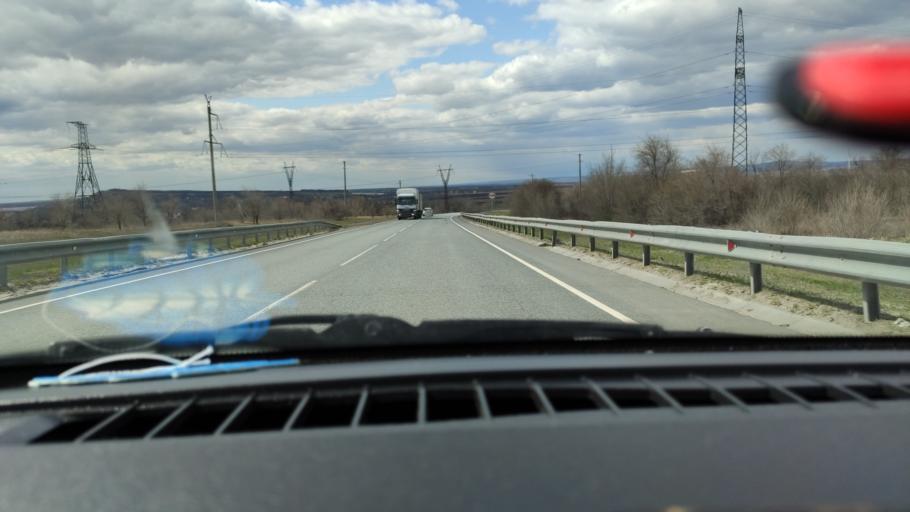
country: RU
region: Saratov
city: Tersa
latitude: 52.0832
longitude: 47.6654
